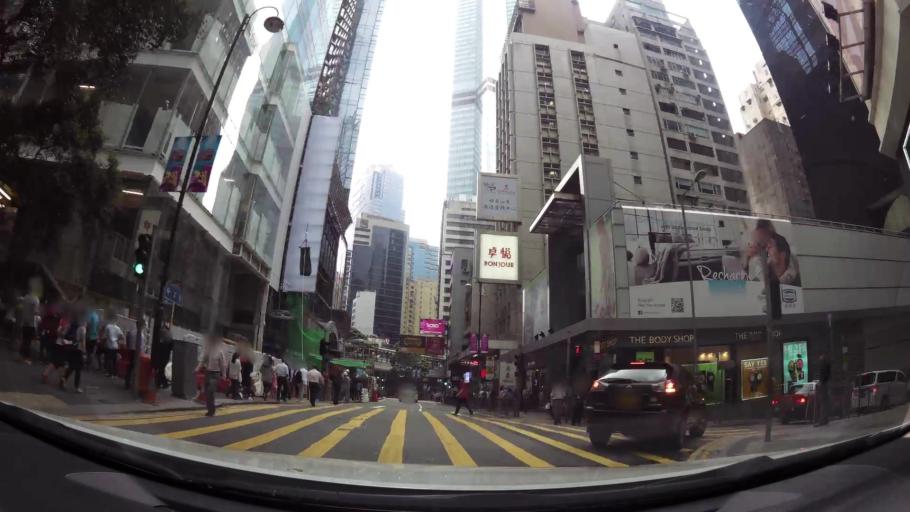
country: HK
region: Central and Western
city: Central
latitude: 22.2829
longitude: 114.1550
